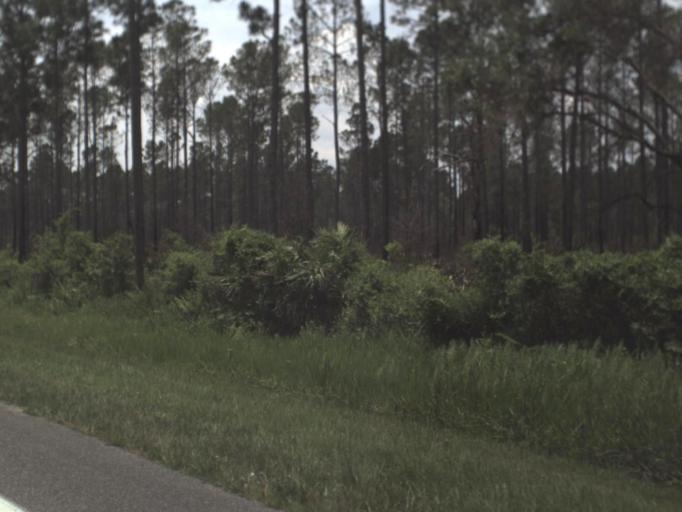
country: US
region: Florida
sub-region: Putnam County
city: Palatka
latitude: 29.5061
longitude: -81.7482
